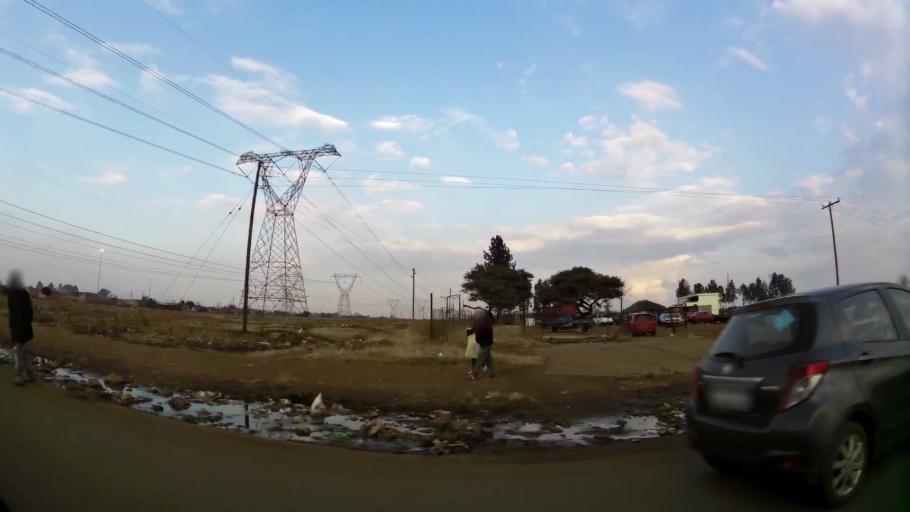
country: ZA
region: Gauteng
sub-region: City of Johannesburg Metropolitan Municipality
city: Orange Farm
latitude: -26.5530
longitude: 27.8311
